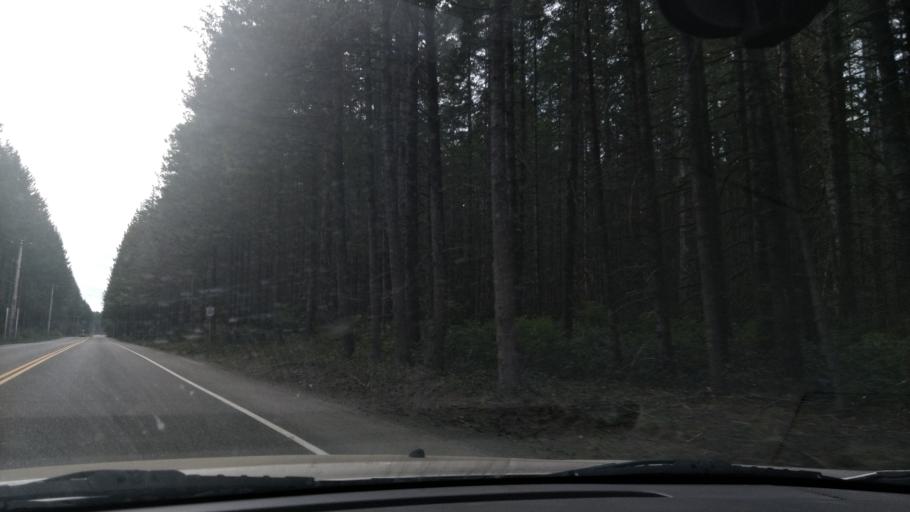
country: CA
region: British Columbia
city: Campbell River
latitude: 50.0341
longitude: -125.3337
